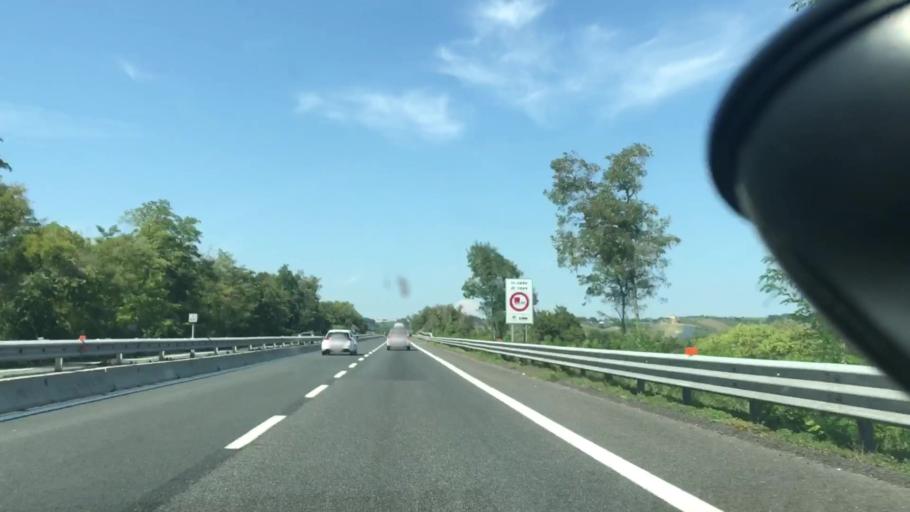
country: IT
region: Abruzzo
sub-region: Provincia di Chieti
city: Torino di Sangro
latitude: 42.2022
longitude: 14.5575
